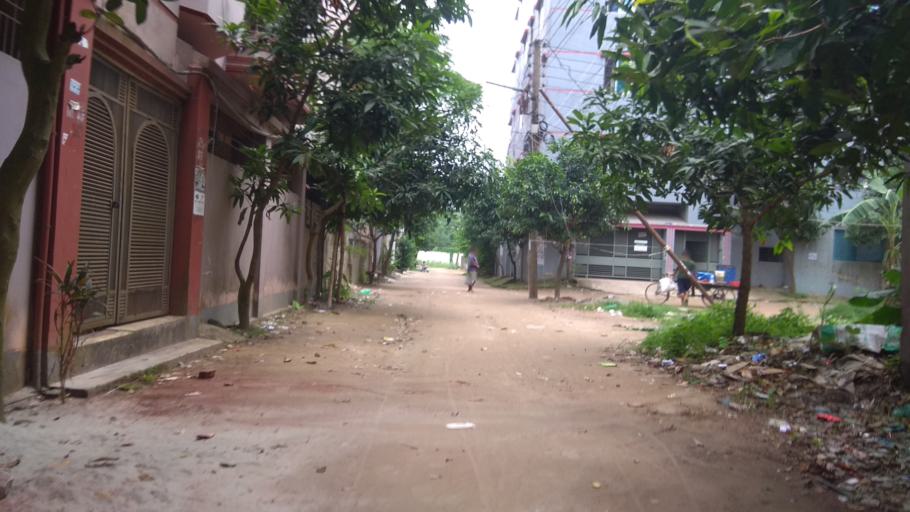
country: BD
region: Dhaka
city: Tungi
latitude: 23.8211
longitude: 90.3525
